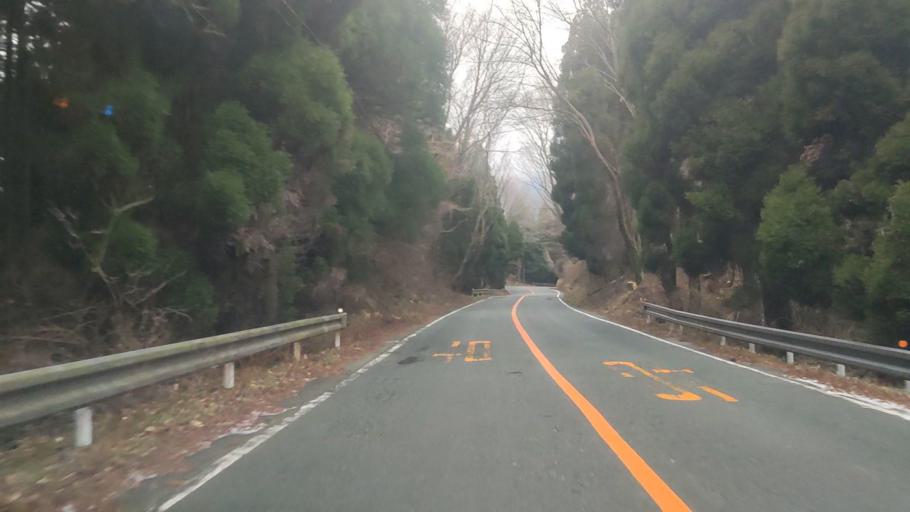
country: JP
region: Kumamoto
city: Aso
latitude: 32.8792
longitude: 131.1740
